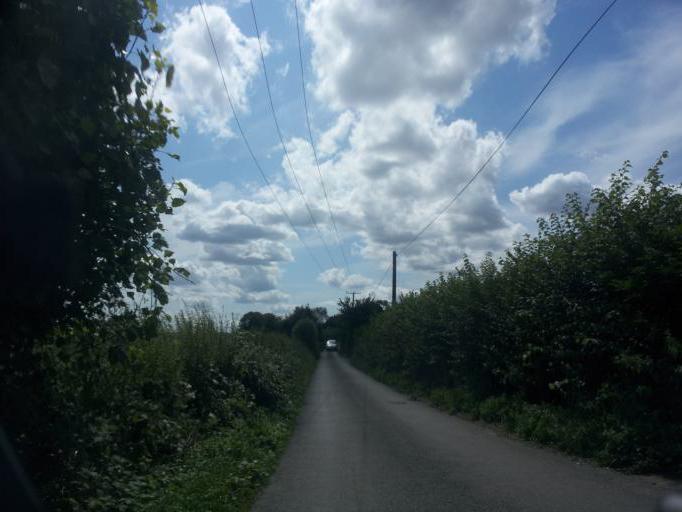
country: GB
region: England
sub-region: Kent
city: Newington
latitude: 51.3720
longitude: 0.6568
